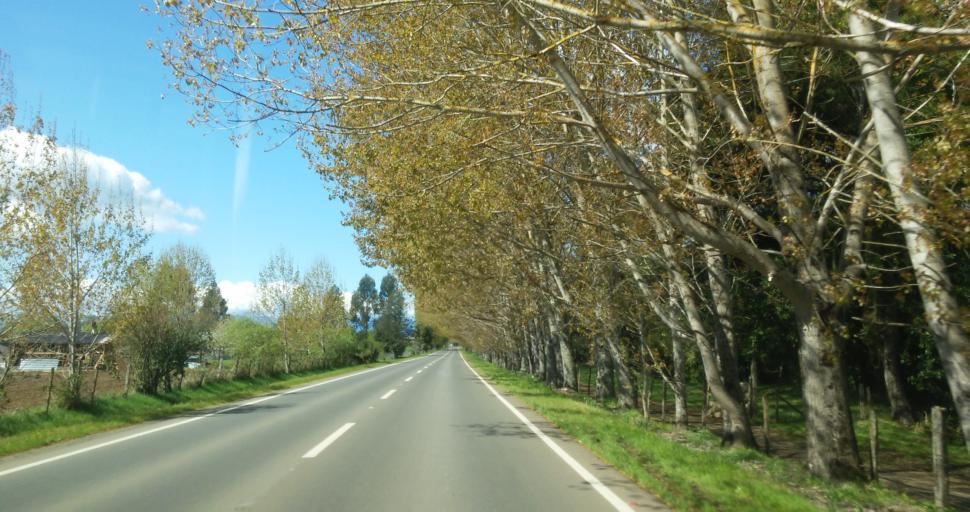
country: CL
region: Los Rios
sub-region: Provincia del Ranco
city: Rio Bueno
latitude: -40.2435
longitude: -72.6153
